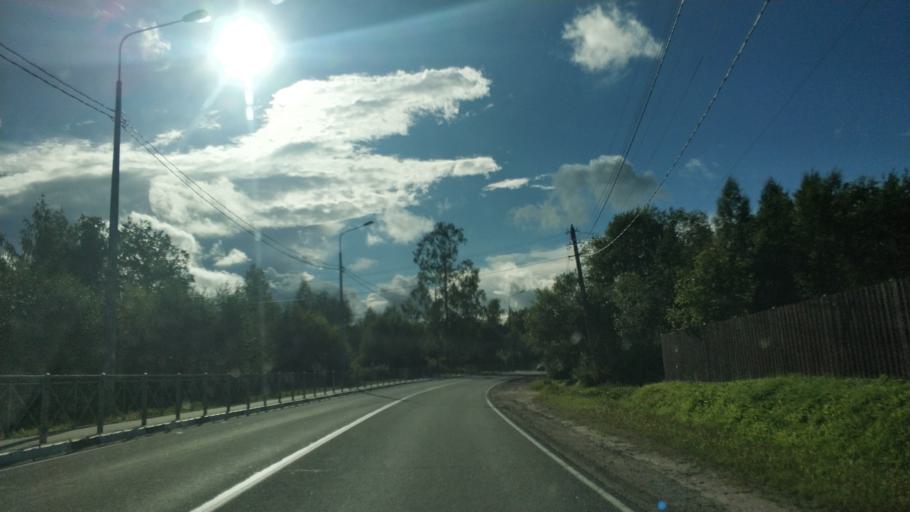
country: RU
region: Republic of Karelia
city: Lakhdenpokh'ya
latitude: 61.5228
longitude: 30.1805
